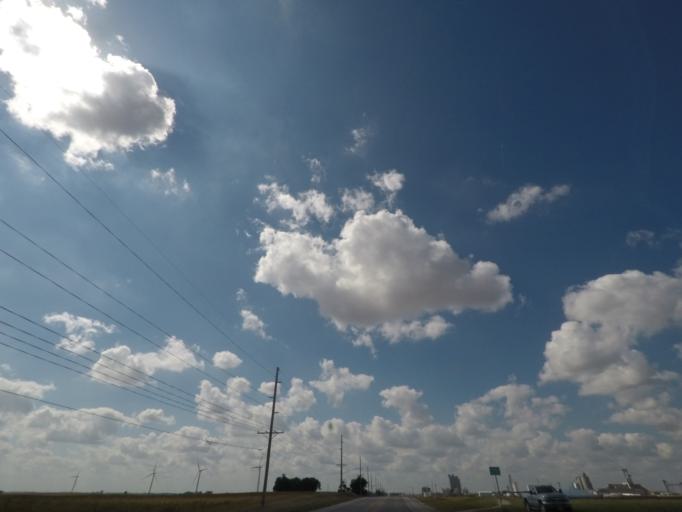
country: US
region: Iowa
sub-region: Story County
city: Nevada
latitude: 42.0231
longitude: -93.4973
